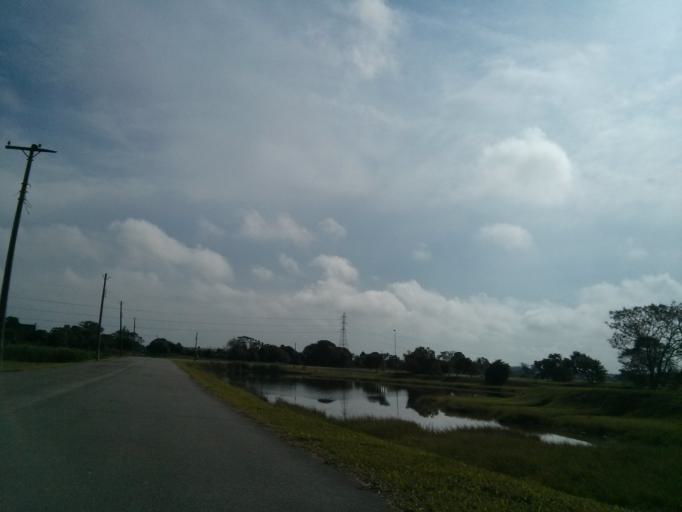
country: BR
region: Parana
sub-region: Sao Jose Dos Pinhais
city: Sao Jose dos Pinhais
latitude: -25.5157
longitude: -49.2177
